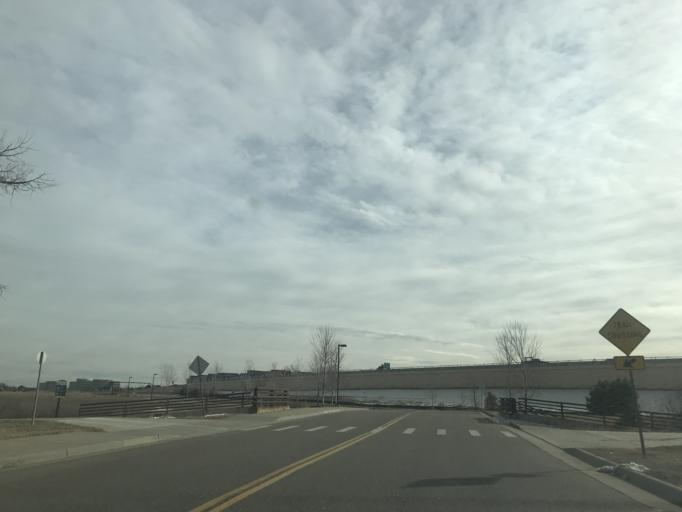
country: US
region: Colorado
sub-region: Arapahoe County
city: Columbine Valley
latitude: 39.5648
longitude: -105.0208
